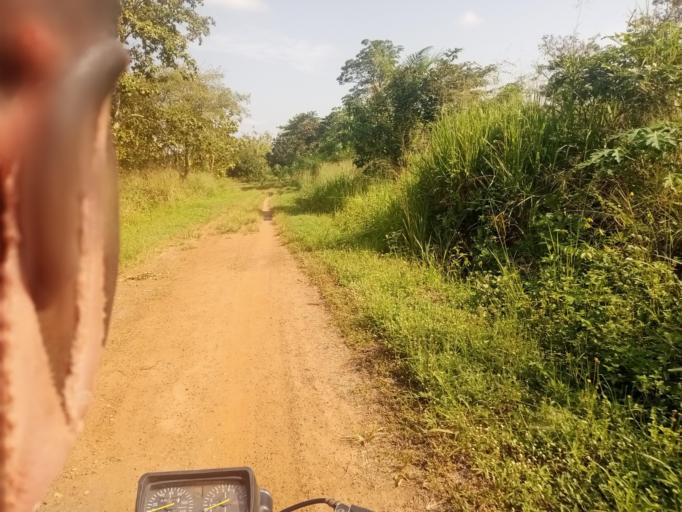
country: TG
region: Maritime
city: Tsevie
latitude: 6.6585
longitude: 0.9722
